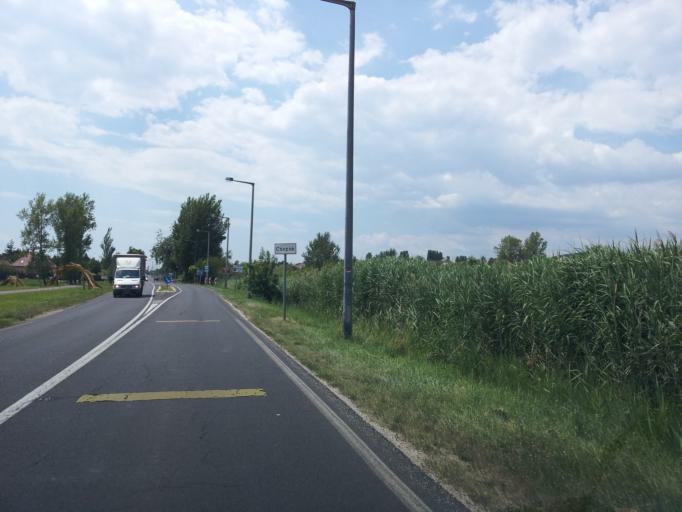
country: HU
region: Veszprem
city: Csopak
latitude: 46.9775
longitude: 17.9370
